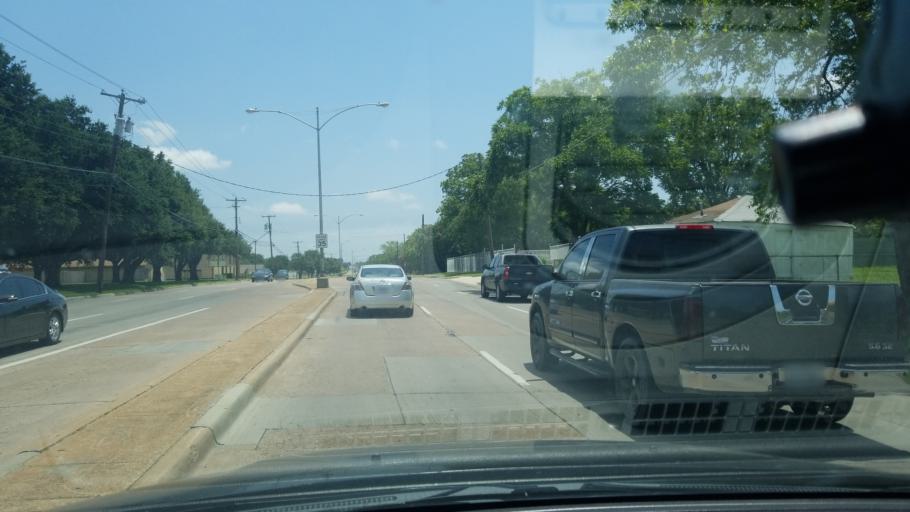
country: US
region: Texas
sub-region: Dallas County
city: Balch Springs
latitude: 32.7488
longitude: -96.6784
